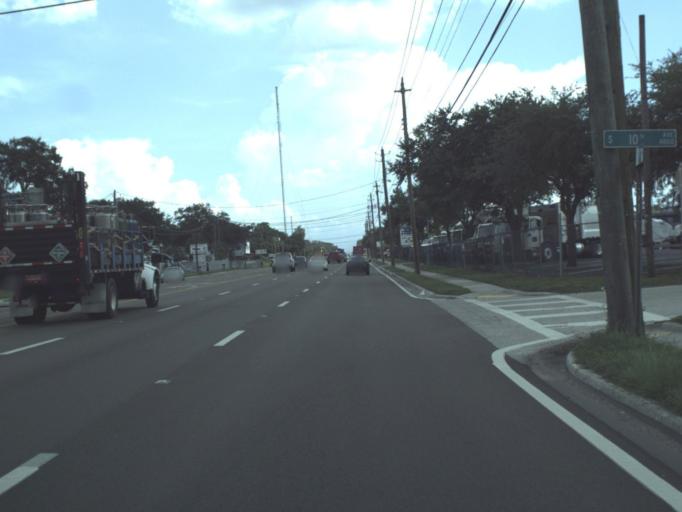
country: US
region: Florida
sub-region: Hillsborough County
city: Palm River-Clair Mel
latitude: 27.9414
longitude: -82.4020
